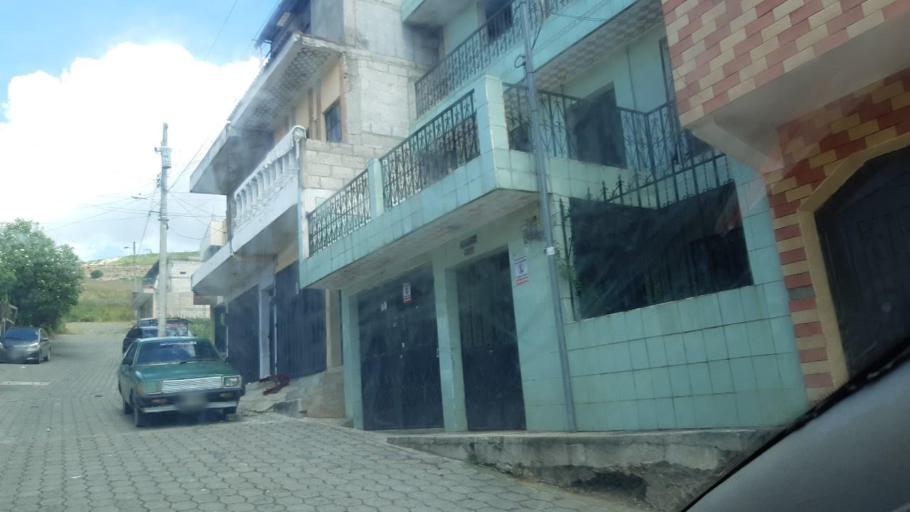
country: GT
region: Quetzaltenango
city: Salcaja
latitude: 14.8795
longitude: -91.4630
